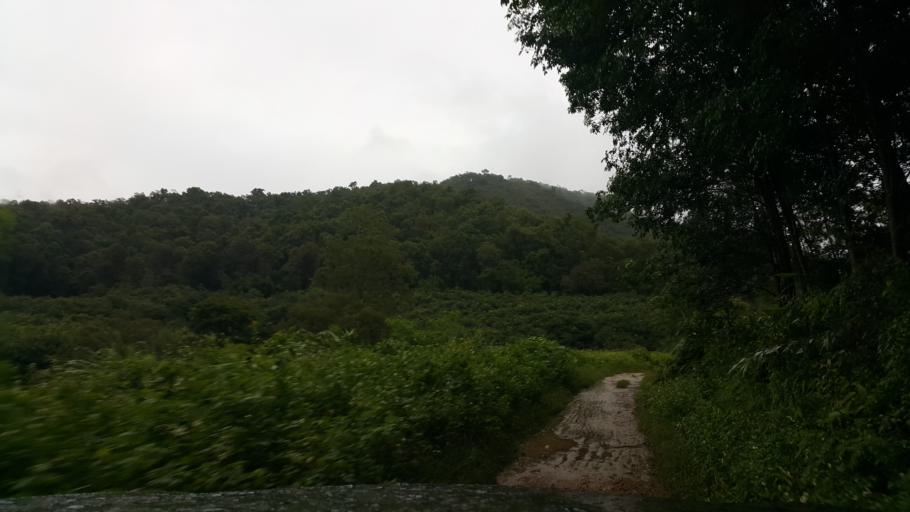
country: TH
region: Phayao
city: Phu Sang
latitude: 19.6248
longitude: 100.4119
